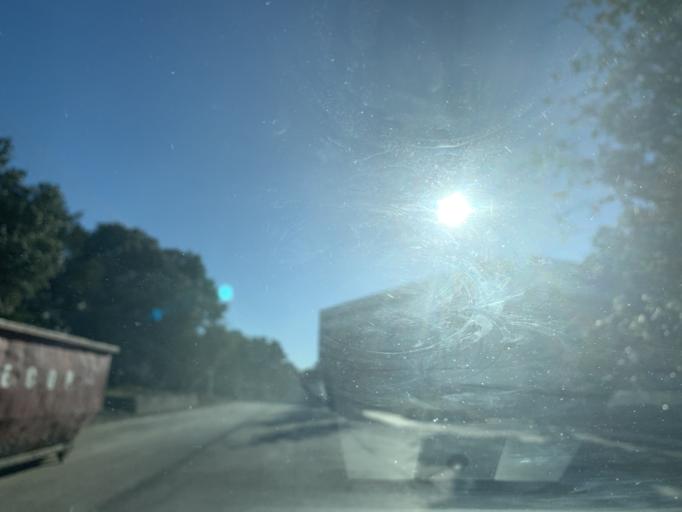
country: US
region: Texas
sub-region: Travis County
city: Wells Branch
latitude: 30.4005
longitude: -97.7095
